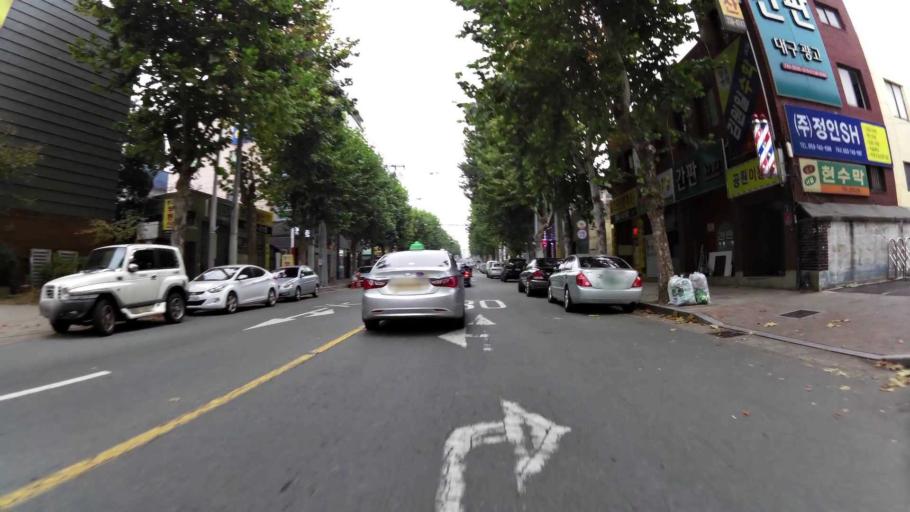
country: KR
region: Daegu
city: Daegu
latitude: 35.8593
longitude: 128.6404
